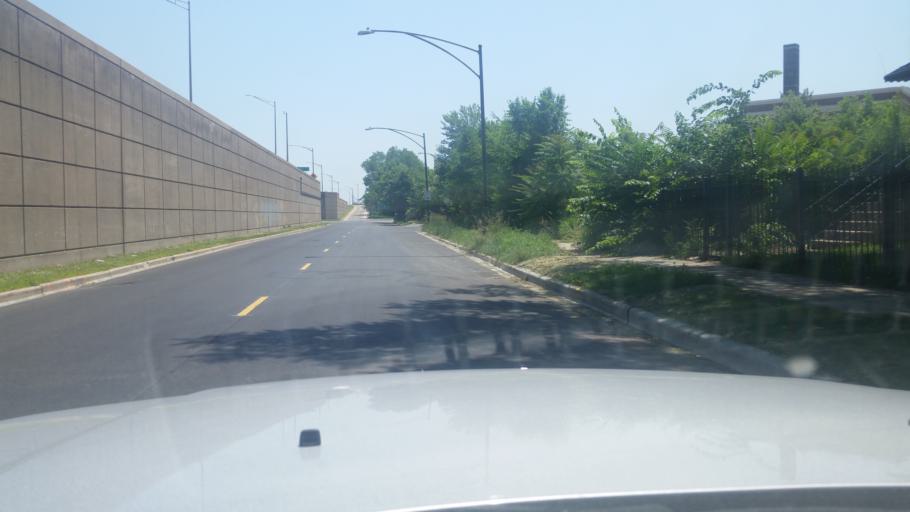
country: US
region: Illinois
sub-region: Cook County
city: Chicago
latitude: 41.7681
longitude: -87.6118
